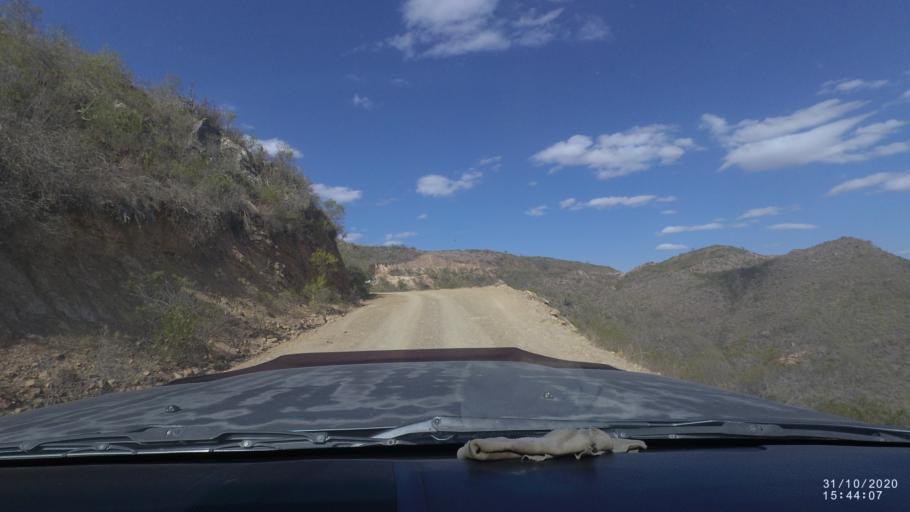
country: BO
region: Chuquisaca
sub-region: Provincia Zudanez
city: Mojocoya
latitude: -18.3192
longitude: -64.7249
